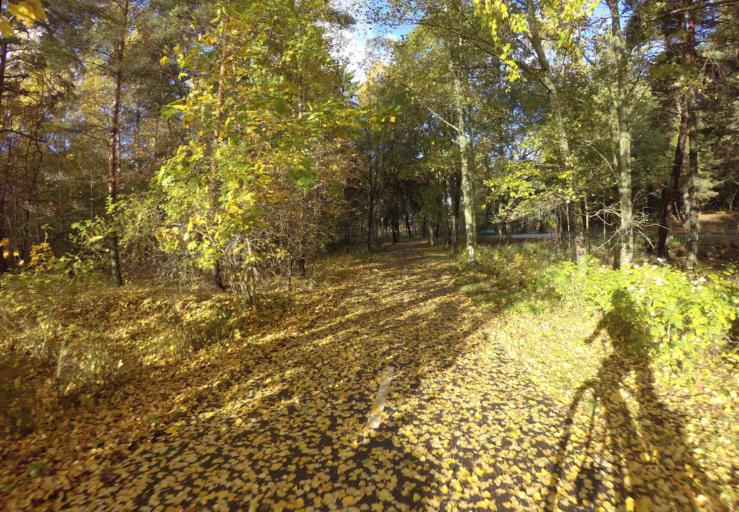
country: FI
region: Varsinais-Suomi
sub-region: Turku
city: Naantali
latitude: 60.4264
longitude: 22.1030
